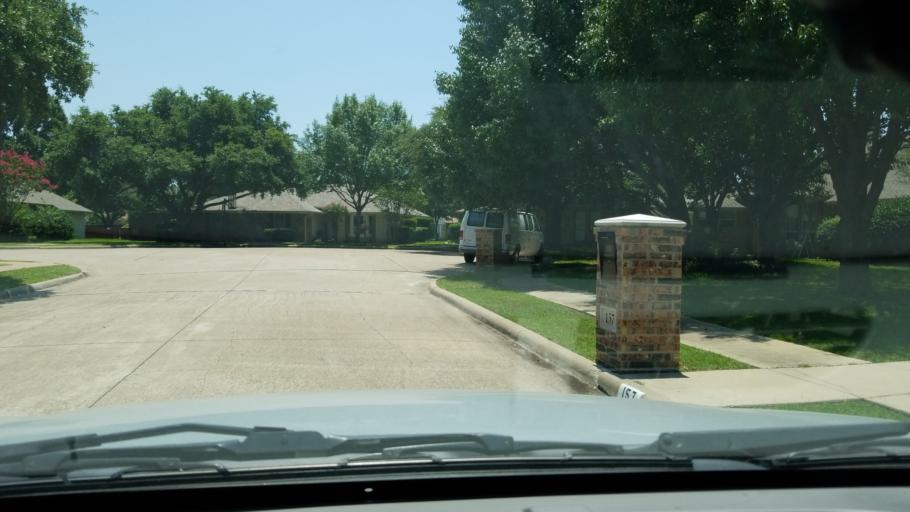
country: US
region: Texas
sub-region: Dallas County
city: Coppell
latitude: 32.9661
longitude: -96.9866
